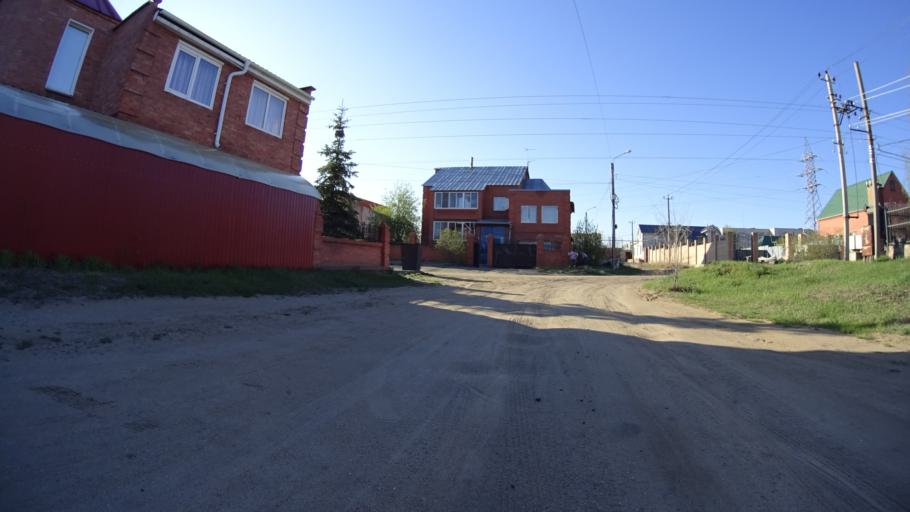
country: RU
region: Chelyabinsk
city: Troitsk
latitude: 54.0699
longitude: 61.5340
